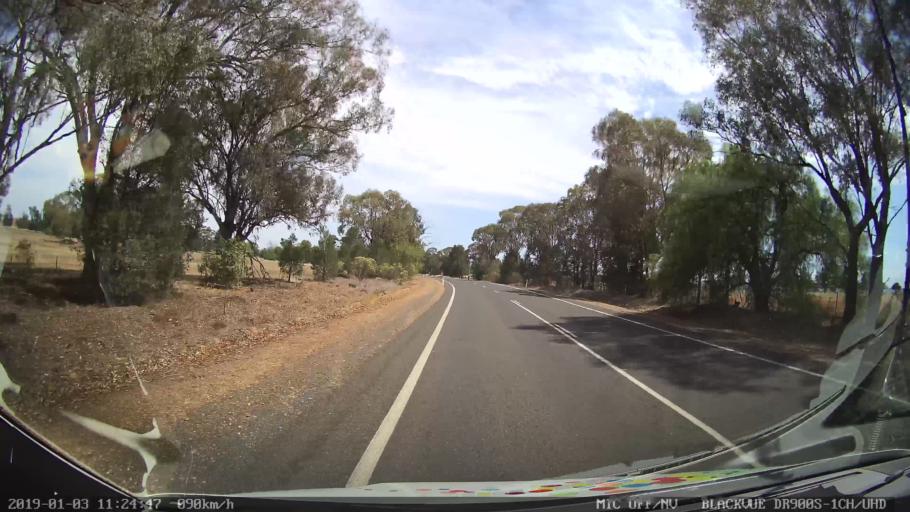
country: AU
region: New South Wales
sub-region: Weddin
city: Grenfell
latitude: -34.0469
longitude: 148.2329
